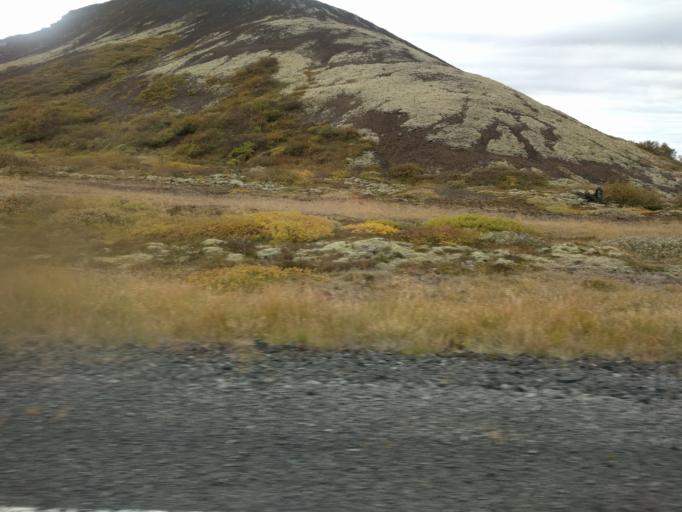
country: IS
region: South
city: Hveragerdi
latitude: 64.1978
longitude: -21.0293
